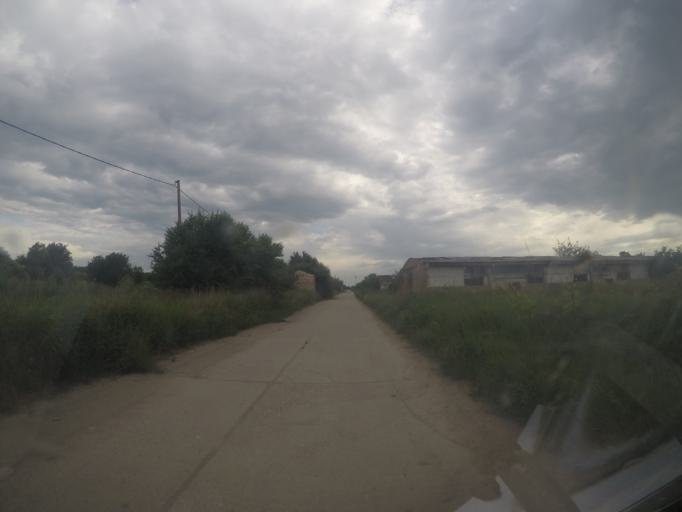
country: RS
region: Central Serbia
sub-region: Belgrade
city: Zemun
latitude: 44.8826
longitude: 20.3835
